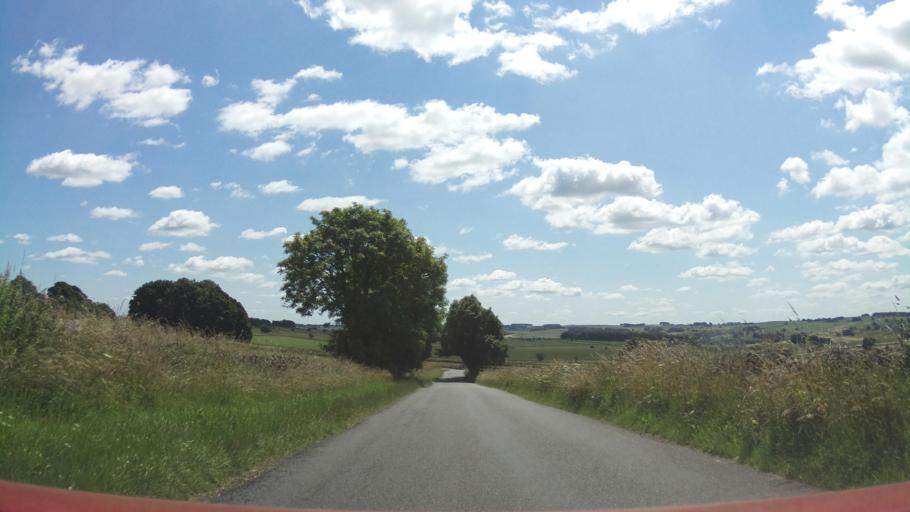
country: GB
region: England
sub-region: Derbyshire
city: Tideswell
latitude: 53.2213
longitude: -1.7801
